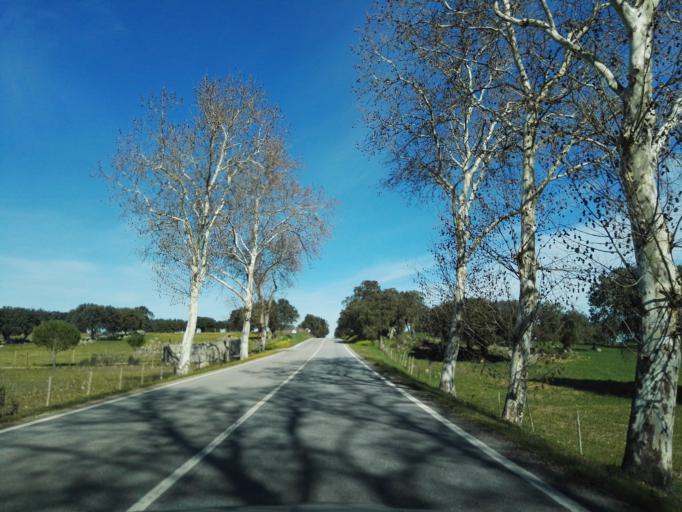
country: PT
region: Portalegre
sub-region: Arronches
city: Arronches
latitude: 39.0924
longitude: -7.2830
